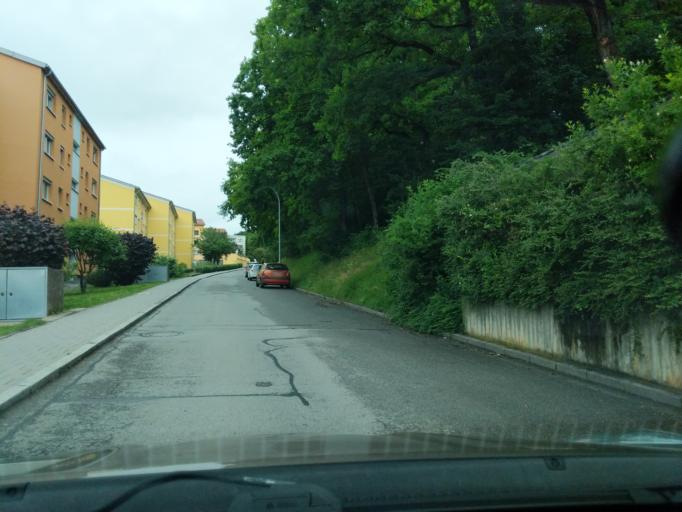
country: DE
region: Bavaria
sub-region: Upper Palatinate
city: Lappersdorf
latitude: 49.0603
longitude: 12.0863
